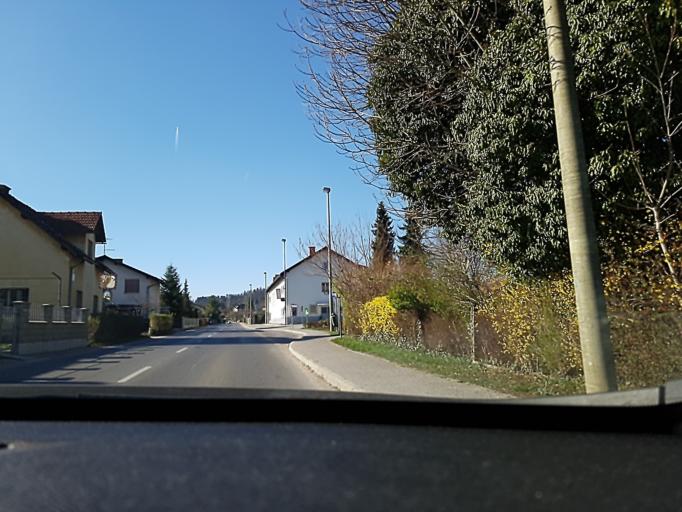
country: SI
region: Medvode
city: Zgornje Pirnice
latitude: 46.1366
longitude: 14.4345
